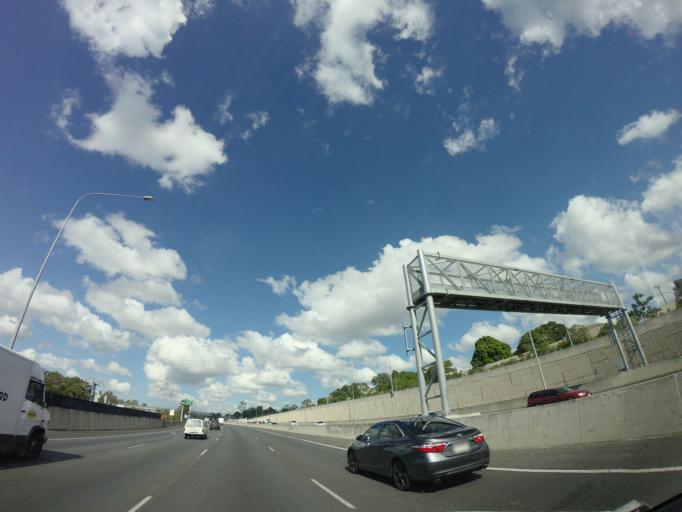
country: AU
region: Queensland
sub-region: Ipswich
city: Goodna
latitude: -27.6086
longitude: 152.9092
